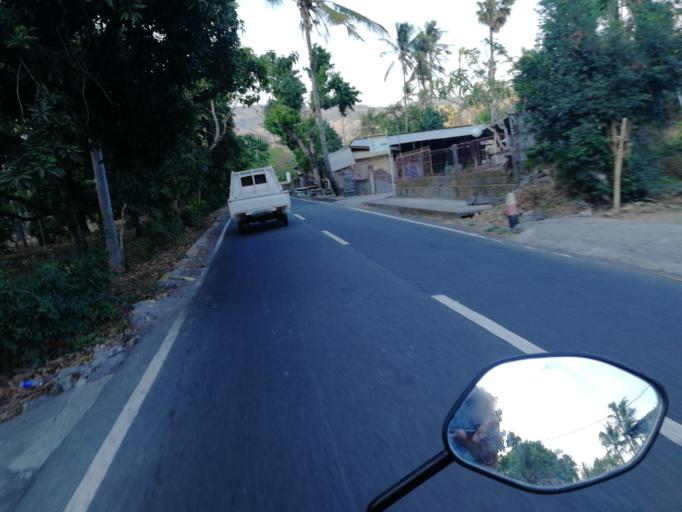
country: ID
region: Bali
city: Banjar Buayang
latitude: -8.3403
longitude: 115.6196
